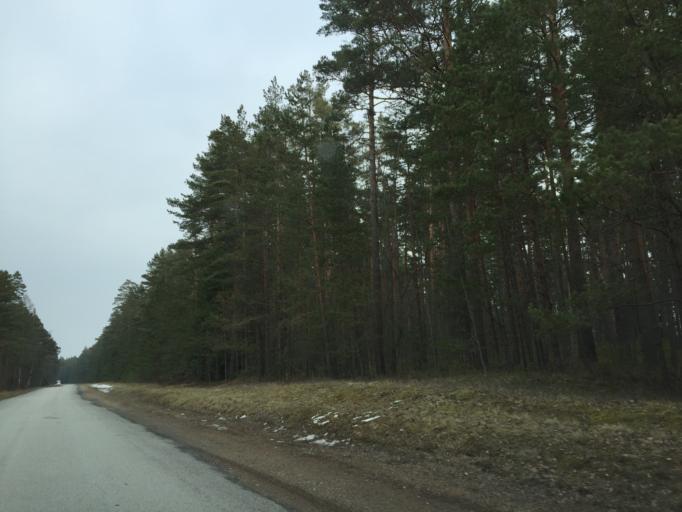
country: LV
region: Salacgrivas
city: Ainazi
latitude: 57.9758
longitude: 24.4128
